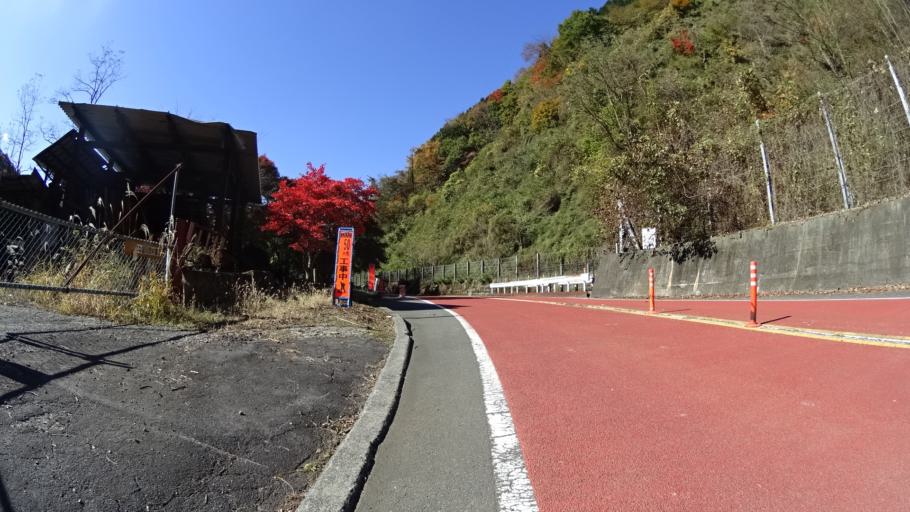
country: JP
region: Yamanashi
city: Uenohara
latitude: 35.7561
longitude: 139.0373
